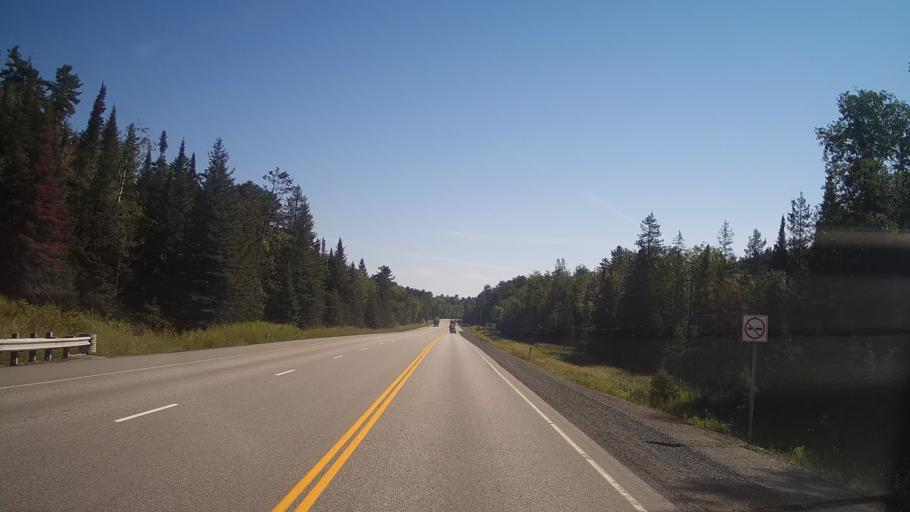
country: CA
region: Ontario
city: Espanola
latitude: 46.2843
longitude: -81.8100
